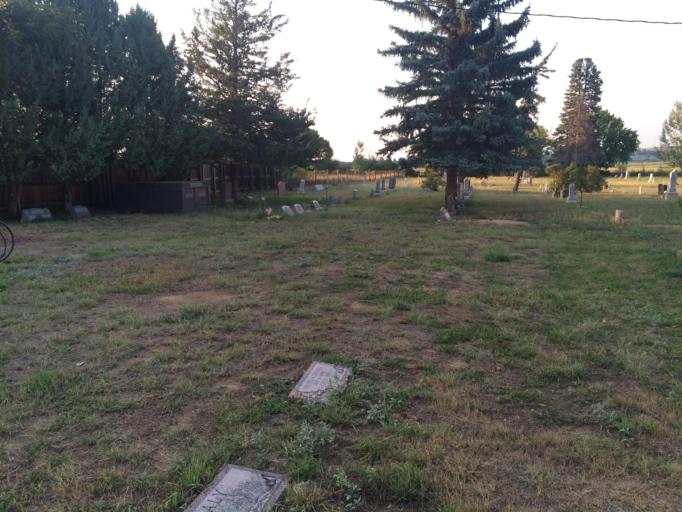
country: US
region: Colorado
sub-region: Boulder County
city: Longmont
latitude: 40.1890
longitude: -105.1692
